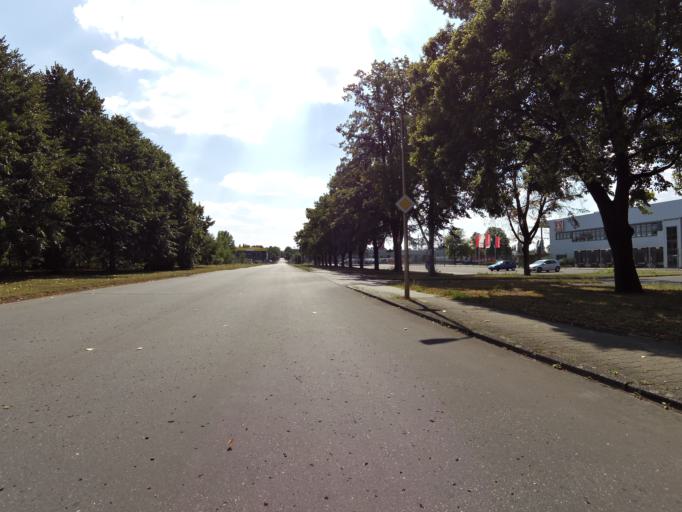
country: DE
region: Berlin
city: Mariendorf
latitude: 52.4431
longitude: 13.3707
